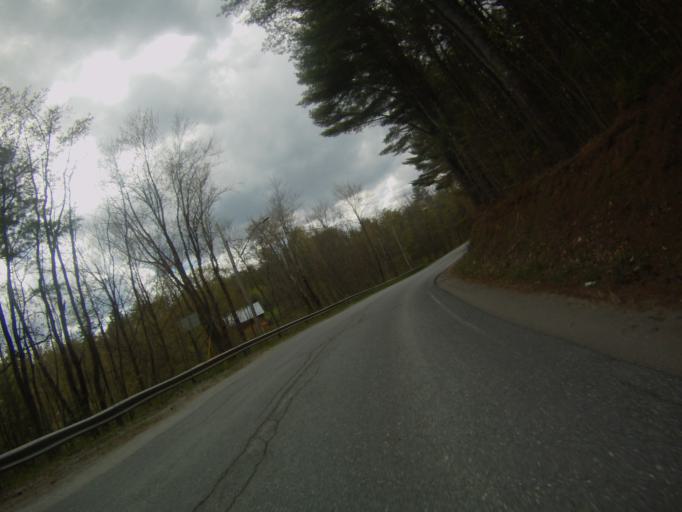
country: US
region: New York
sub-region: Essex County
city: Mineville
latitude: 44.0900
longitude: -73.5458
